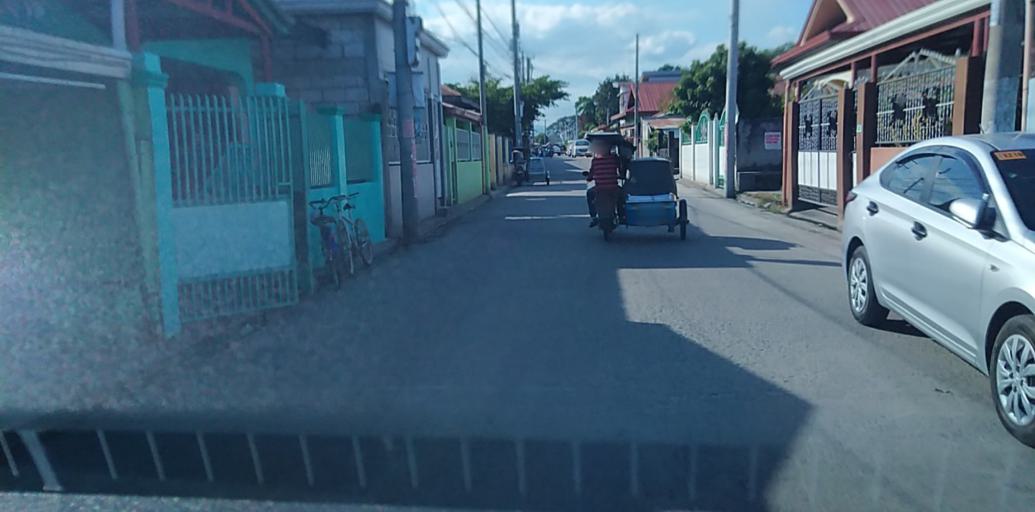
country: PH
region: Central Luzon
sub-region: Province of Pampanga
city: Acli
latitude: 15.1151
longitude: 120.6376
